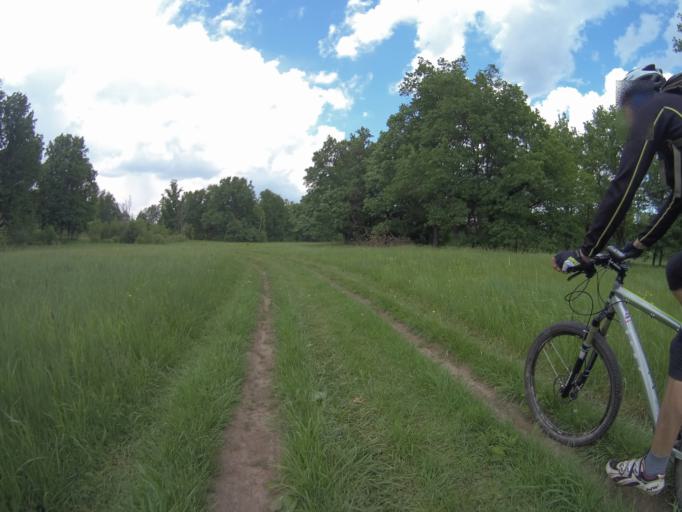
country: RU
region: Vladimir
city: Vorsha
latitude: 56.0299
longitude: 40.2044
